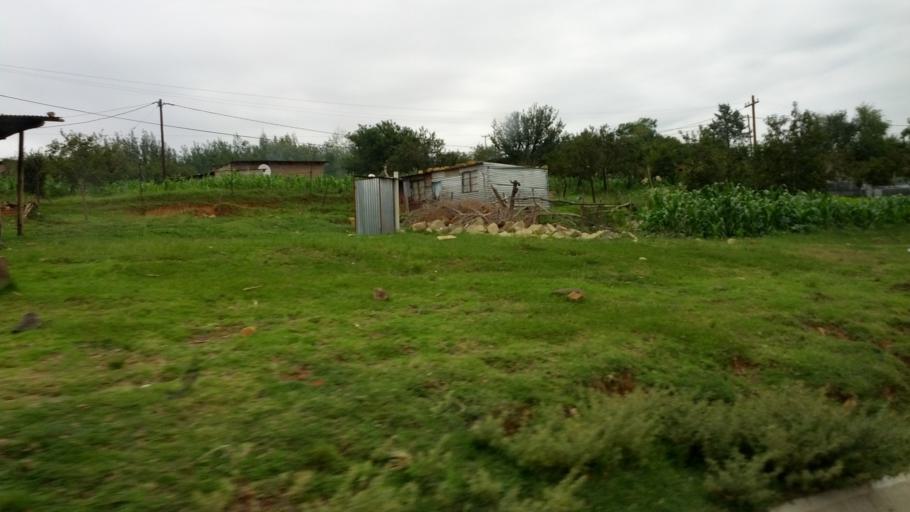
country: LS
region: Berea
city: Teyateyaneng
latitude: -29.1311
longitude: 27.9858
